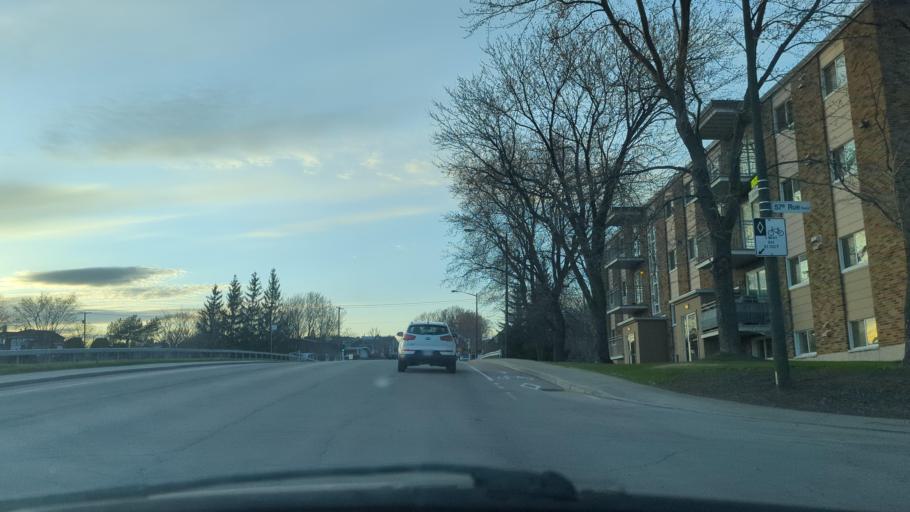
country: CA
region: Quebec
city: Quebec
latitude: 46.8488
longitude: -71.2607
